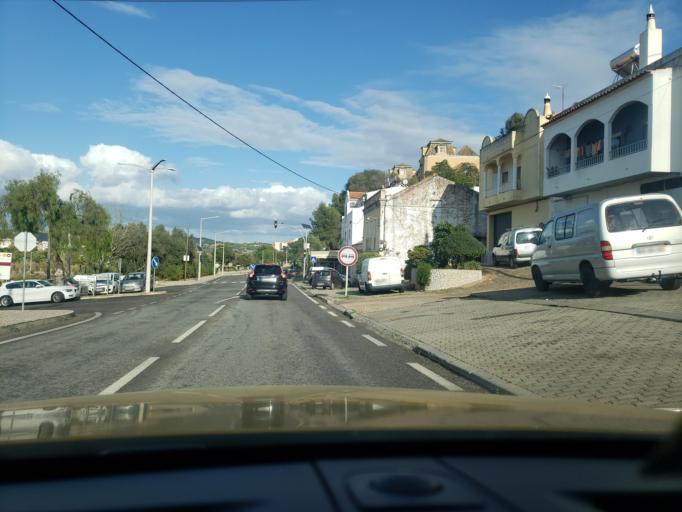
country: PT
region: Faro
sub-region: Silves
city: Silves
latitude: 37.1851
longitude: -8.4371
